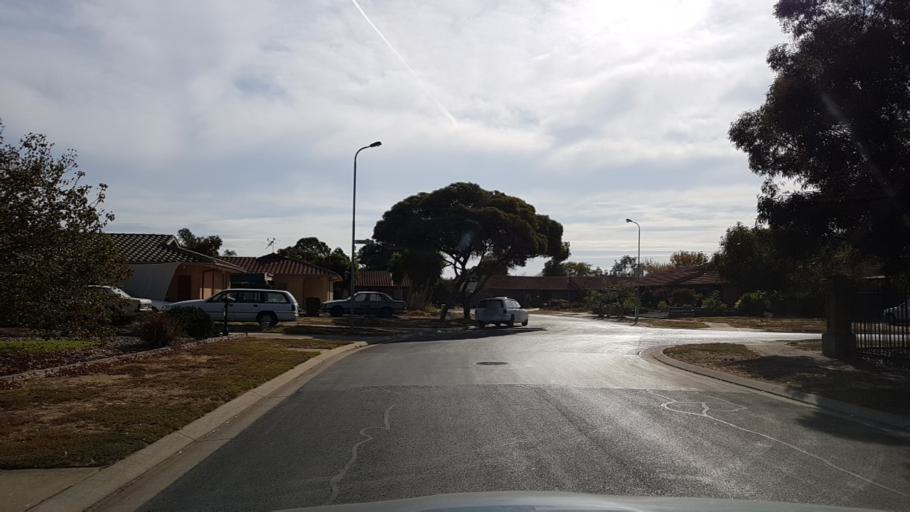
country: AU
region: South Australia
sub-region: Charles Sturt
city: West Lakes Shore
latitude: -34.8544
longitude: 138.4963
